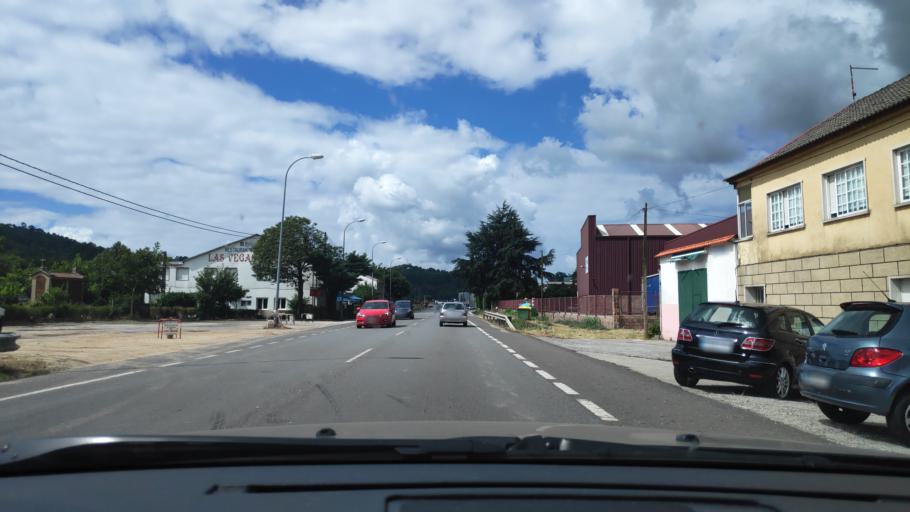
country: ES
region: Galicia
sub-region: Provincia de Pontevedra
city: Portas
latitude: 42.5991
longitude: -8.6629
